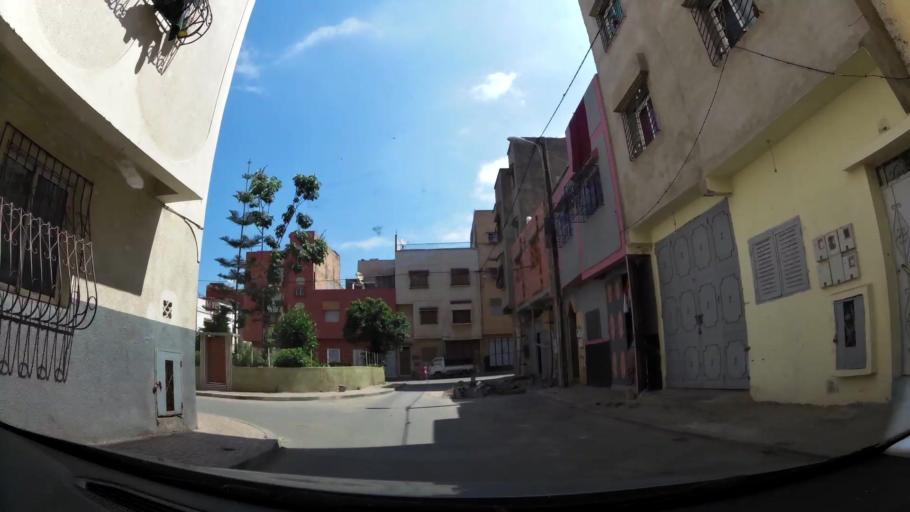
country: MA
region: Rabat-Sale-Zemmour-Zaer
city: Sale
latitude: 34.0647
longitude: -6.7844
